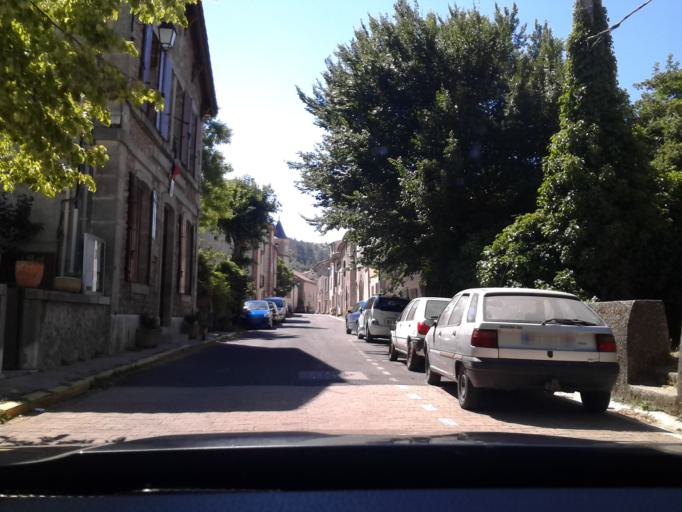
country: FR
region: Languedoc-Roussillon
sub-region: Departement de l'Herault
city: Montpeyroux
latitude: 43.7901
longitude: 3.4593
